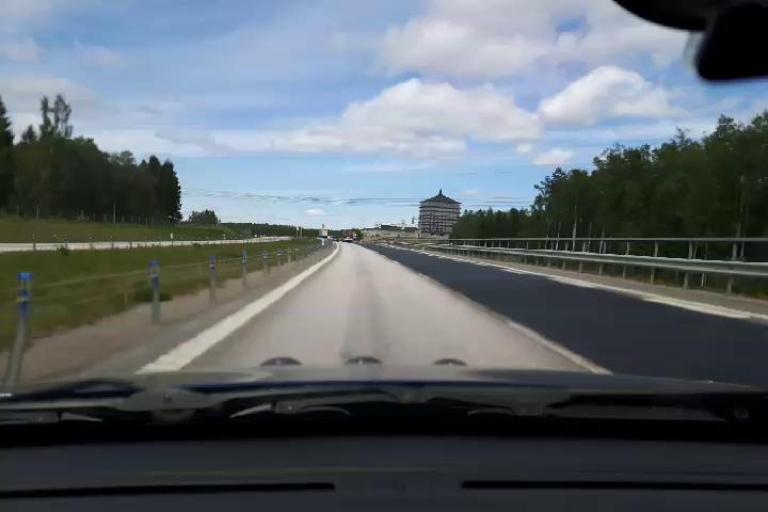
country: SE
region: Uppsala
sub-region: Alvkarleby Kommun
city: AElvkarleby
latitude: 60.4584
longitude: 17.4150
